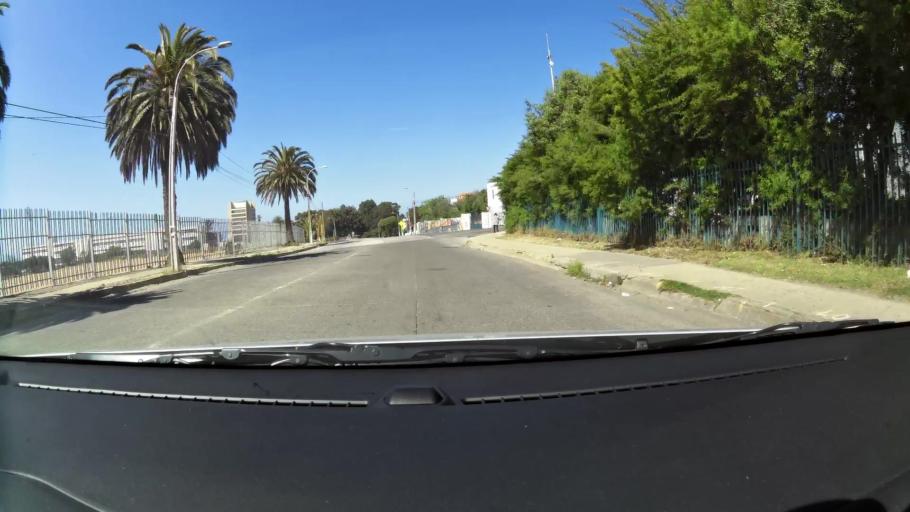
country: CL
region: Valparaiso
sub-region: Provincia de Valparaiso
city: Valparaiso
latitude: -33.0247
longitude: -71.6387
